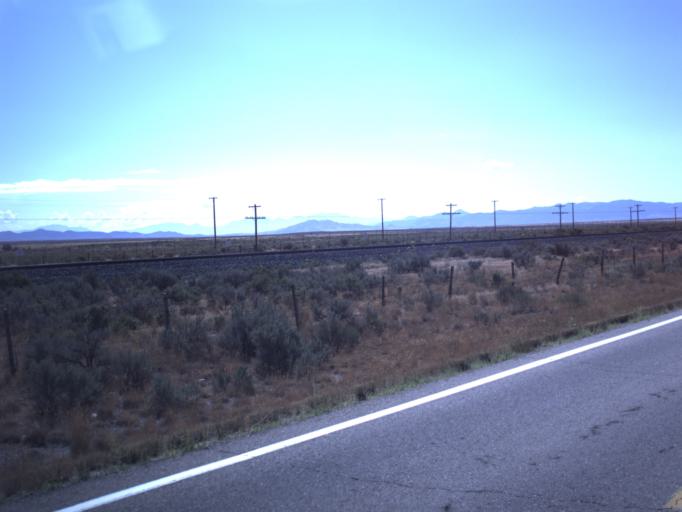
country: US
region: Utah
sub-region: Tooele County
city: Tooele
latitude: 40.2901
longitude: -112.4005
